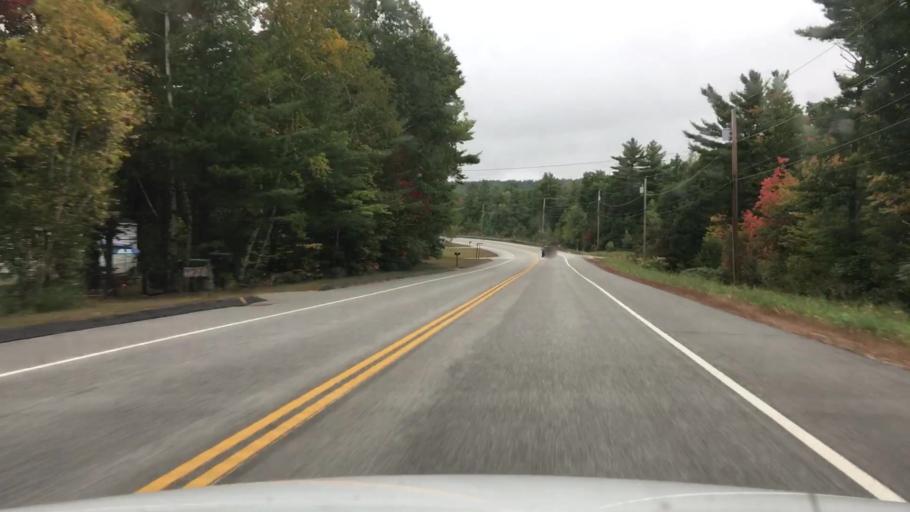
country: US
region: Maine
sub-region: Androscoggin County
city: Poland
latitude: 44.0505
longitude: -70.3802
